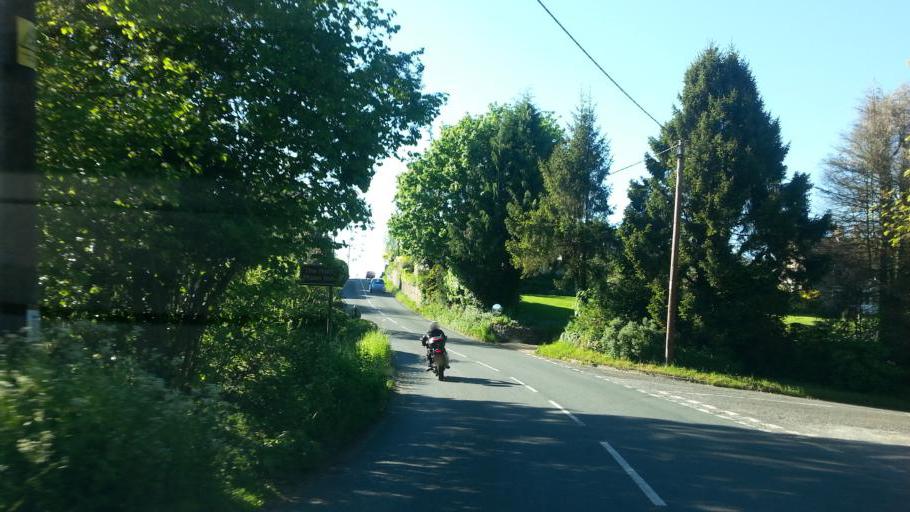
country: GB
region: England
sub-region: Somerset
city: Wincanton
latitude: 51.0116
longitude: -2.4294
